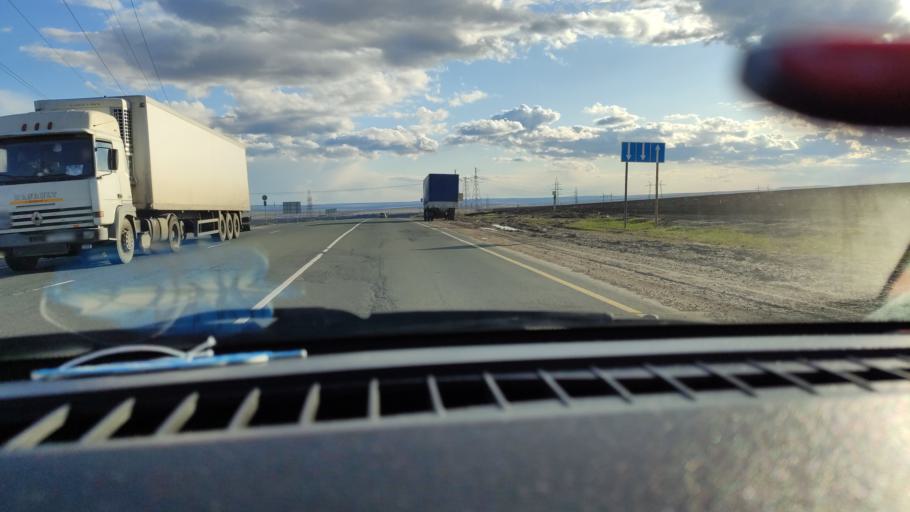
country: RU
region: Saratov
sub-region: Saratovskiy Rayon
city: Saratov
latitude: 51.7665
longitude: 46.0777
